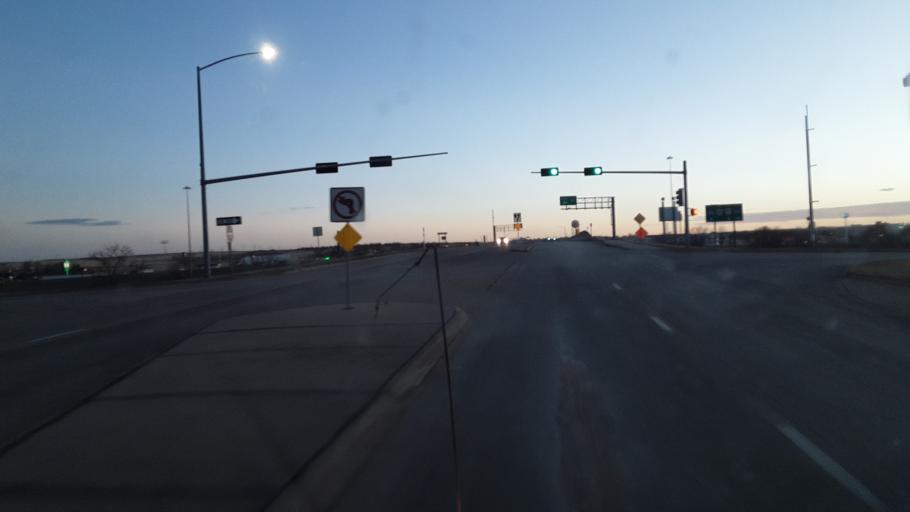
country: US
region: Nebraska
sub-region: Keith County
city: Ogallala
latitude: 41.1170
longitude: -101.7147
